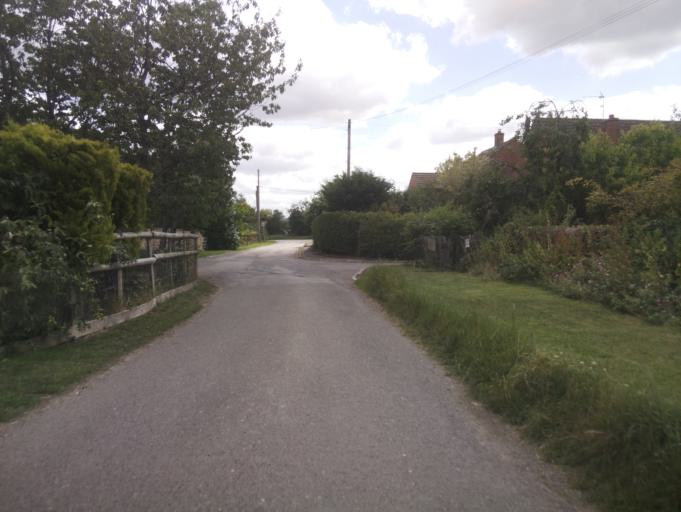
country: GB
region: England
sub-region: Oxfordshire
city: Faringdon
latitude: 51.6166
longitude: -1.6024
